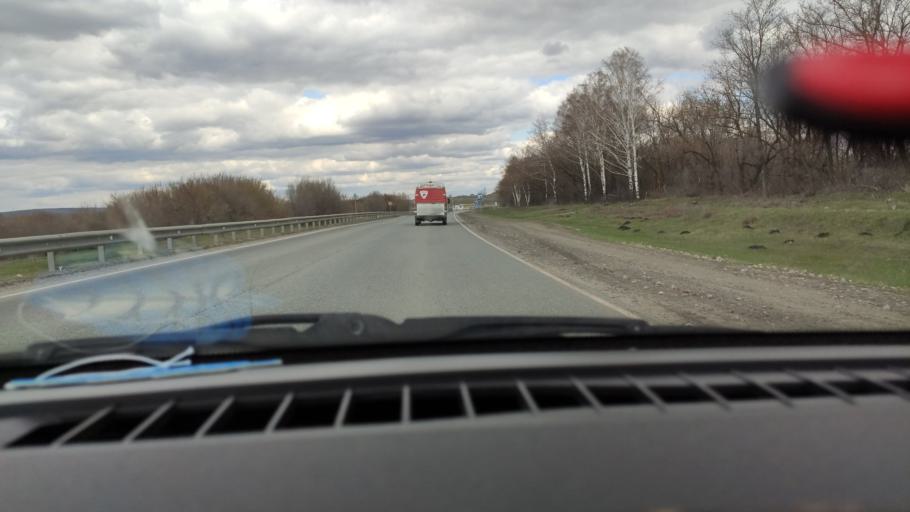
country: RU
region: Saratov
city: Tersa
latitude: 52.0933
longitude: 47.5426
